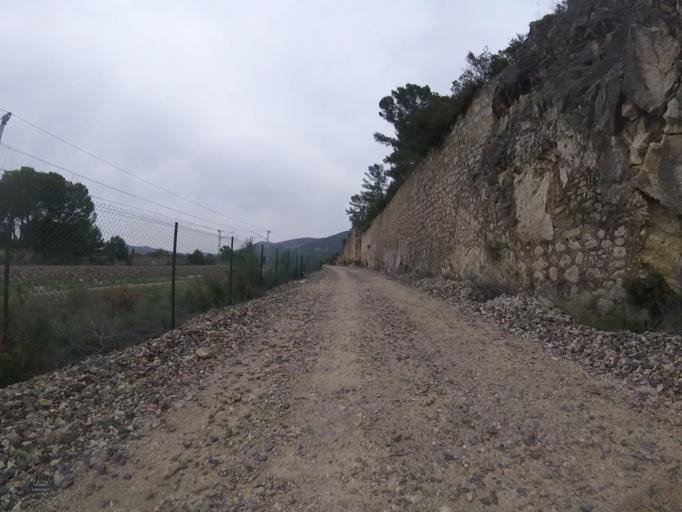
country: ES
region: Valencia
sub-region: Provincia de Castello
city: Alcoceber
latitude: 40.2516
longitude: 0.2486
